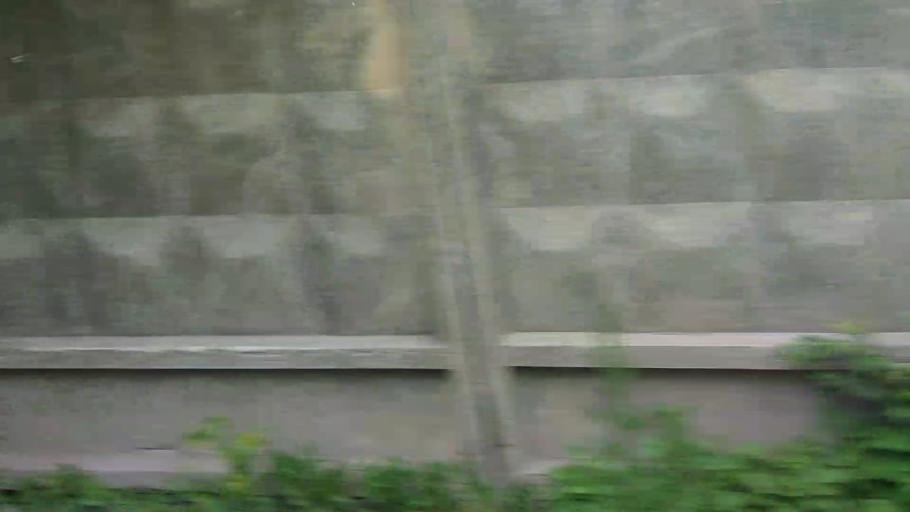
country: RU
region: Moskovskaya
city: Ramenskoye
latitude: 55.5665
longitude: 38.2602
